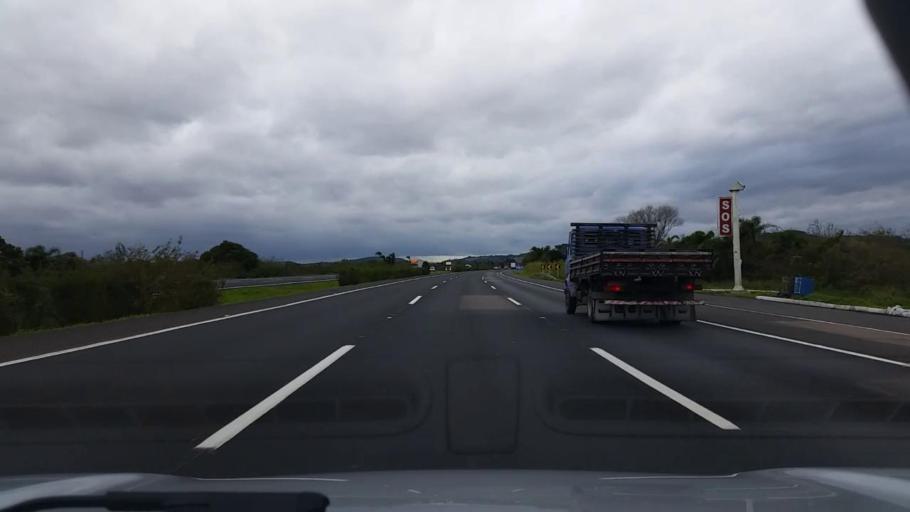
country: BR
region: Rio Grande do Sul
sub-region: Osorio
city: Osorio
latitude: -29.8810
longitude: -50.4348
